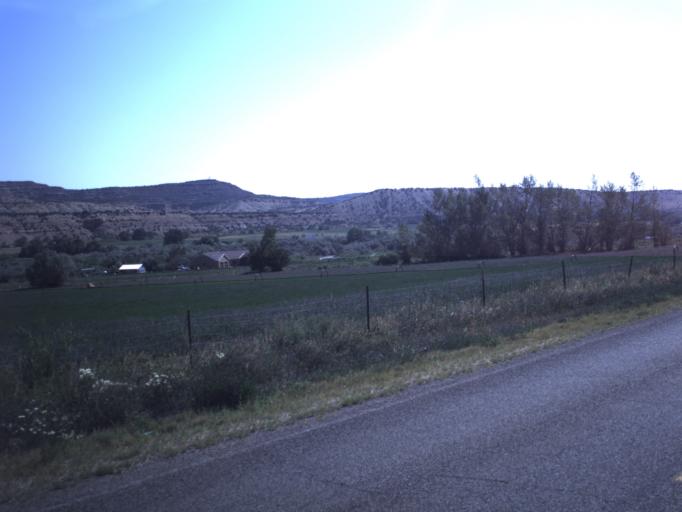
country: US
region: Utah
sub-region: Duchesne County
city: Duchesne
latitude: 40.2720
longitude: -110.4529
